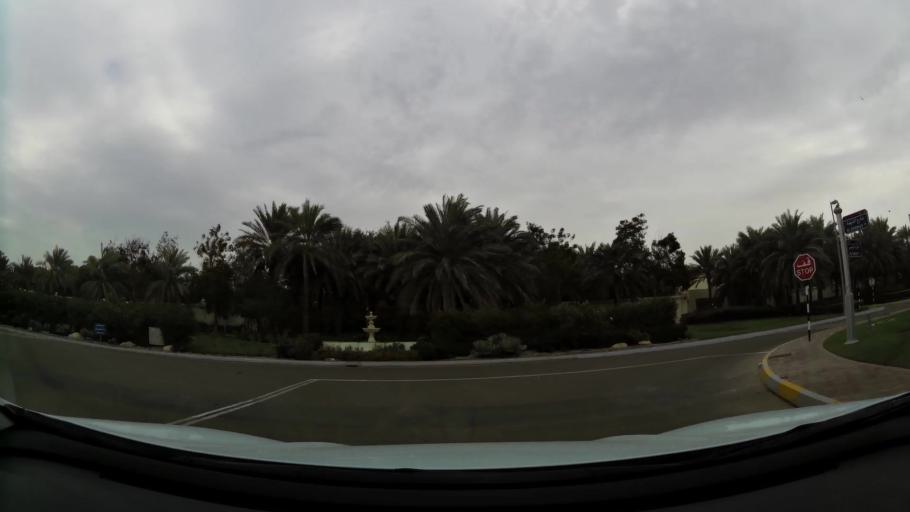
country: AE
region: Abu Dhabi
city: Abu Dhabi
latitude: 24.4068
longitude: 54.4482
